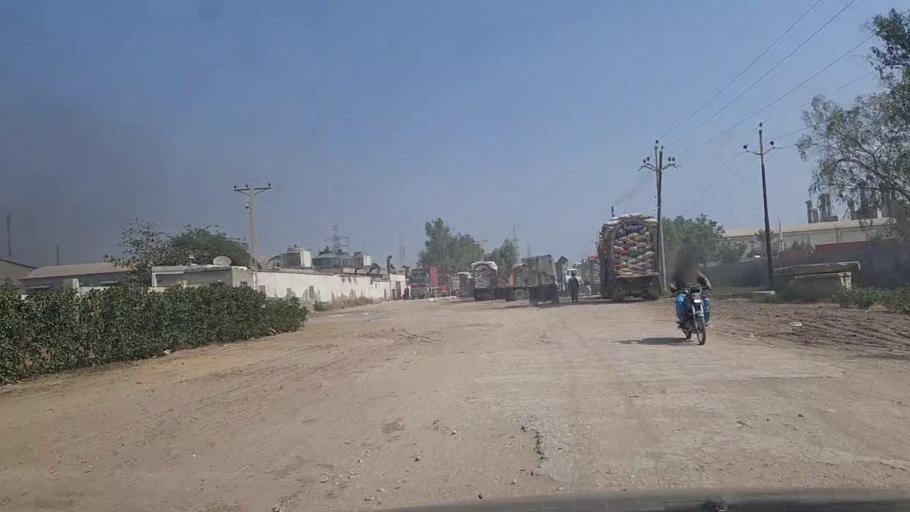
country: PK
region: Sindh
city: Gharo
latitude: 24.7381
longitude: 67.6040
